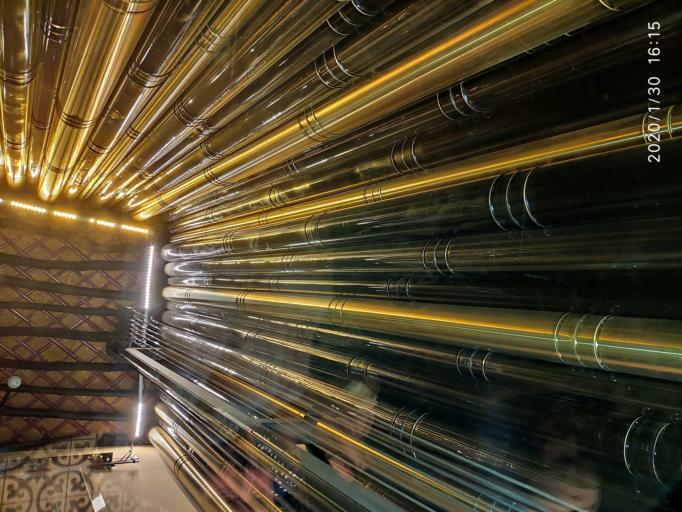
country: QA
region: Baladiyat ad Dawhah
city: Doha
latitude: 25.2868
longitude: 51.5326
